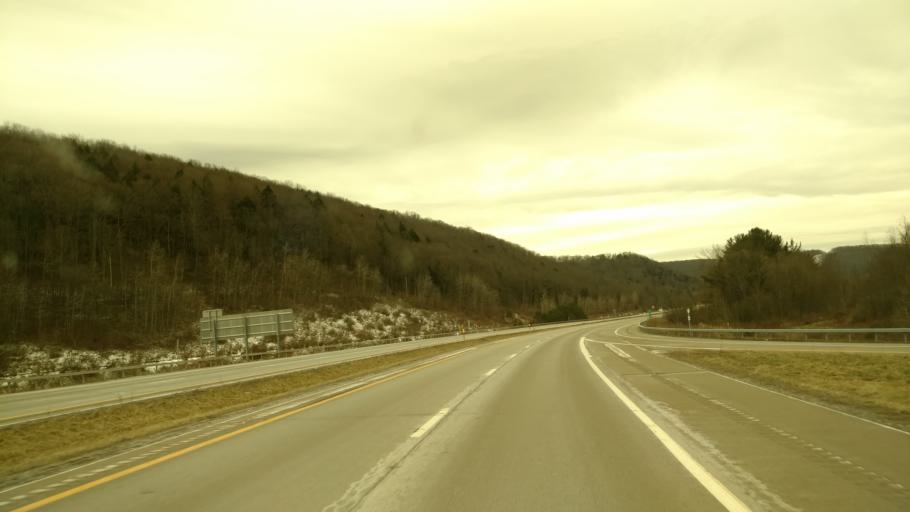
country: US
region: New York
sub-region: Cattaraugus County
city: Salamanca
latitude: 42.1080
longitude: -78.7814
